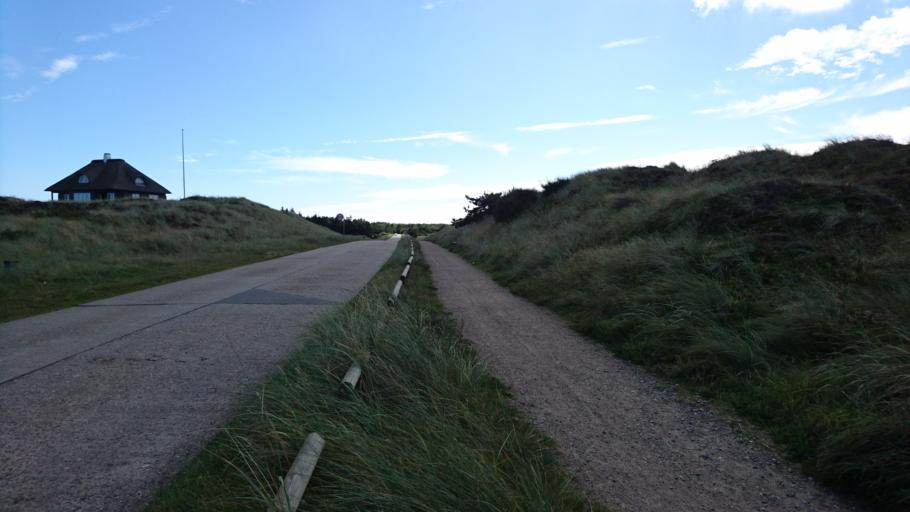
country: DK
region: North Denmark
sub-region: Frederikshavn Kommune
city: Skagen
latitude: 57.7249
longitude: 10.5265
